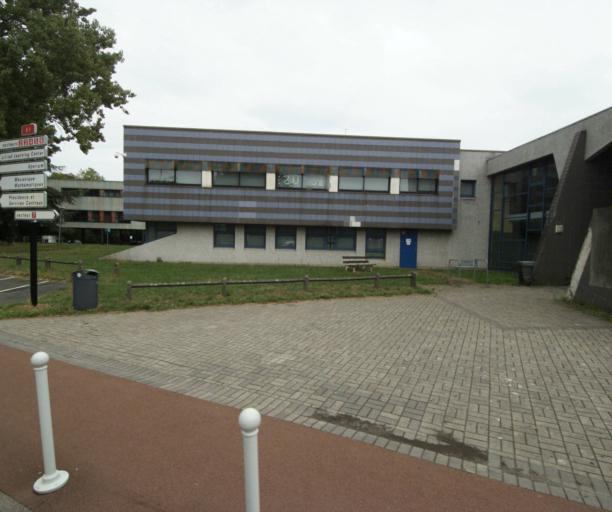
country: FR
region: Nord-Pas-de-Calais
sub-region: Departement du Nord
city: Lezennes
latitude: 50.6099
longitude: 3.1364
